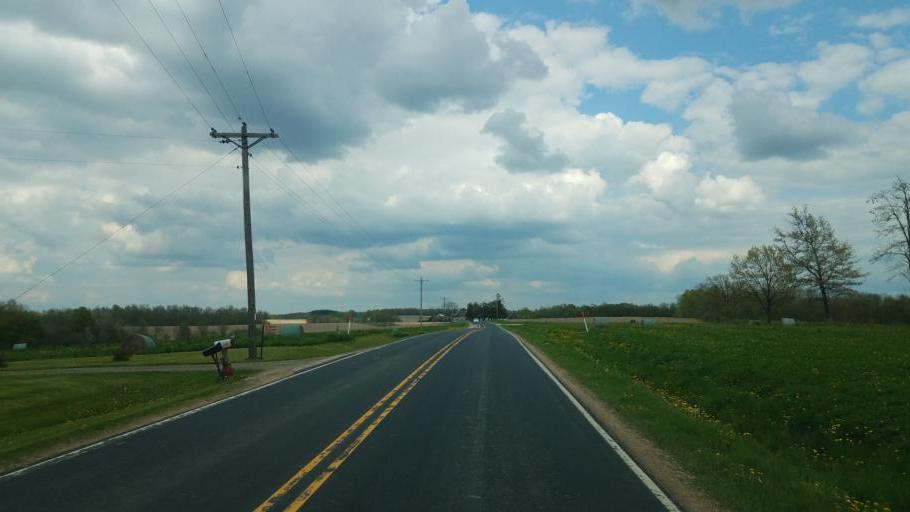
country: US
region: Wisconsin
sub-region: Vernon County
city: Hillsboro
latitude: 43.5908
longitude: -90.3343
